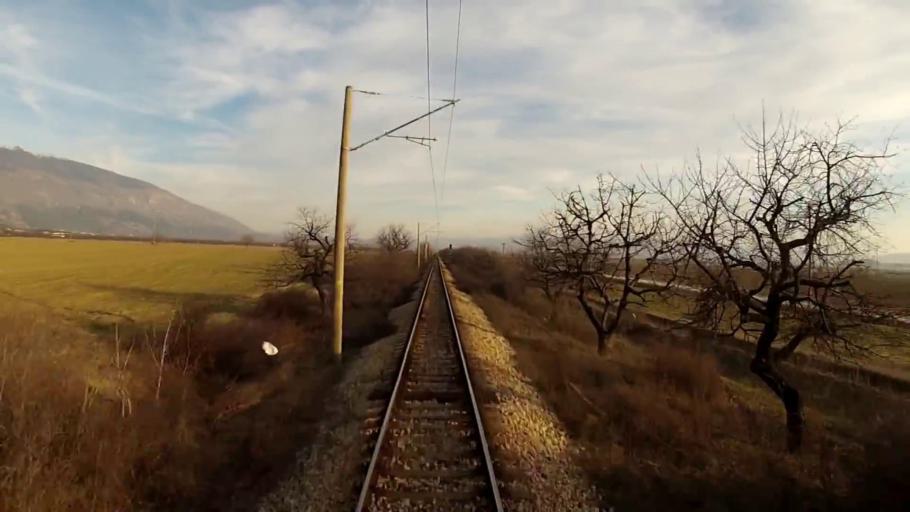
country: BG
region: Plovdiv
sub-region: Obshtina Karlovo
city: Karlovo
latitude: 42.6357
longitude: 24.7639
